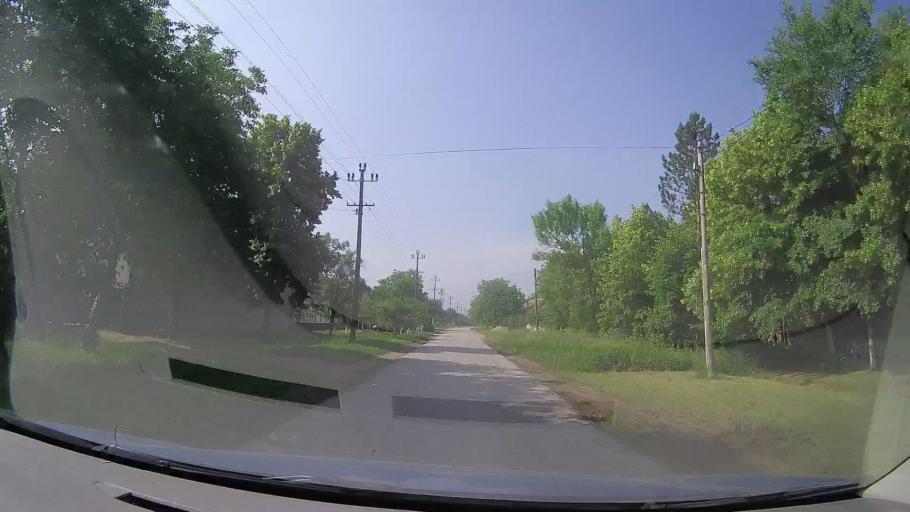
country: RS
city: Jasa Tomic
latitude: 45.4434
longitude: 20.8524
